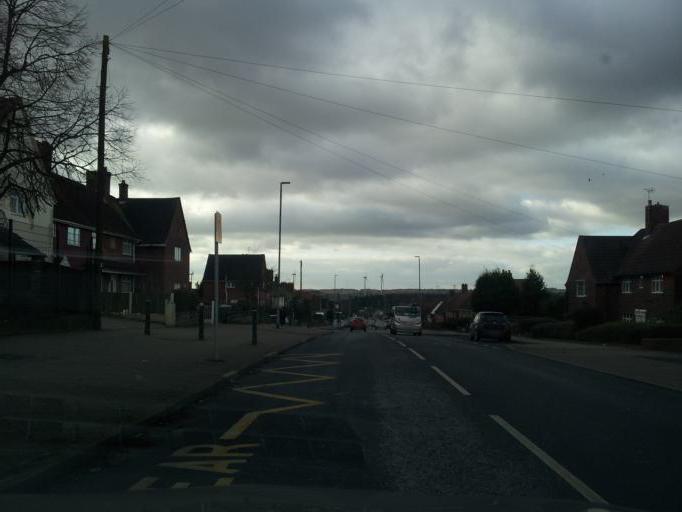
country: GB
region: England
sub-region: Nottinghamshire
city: Rainworth
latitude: 53.1192
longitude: -1.1091
